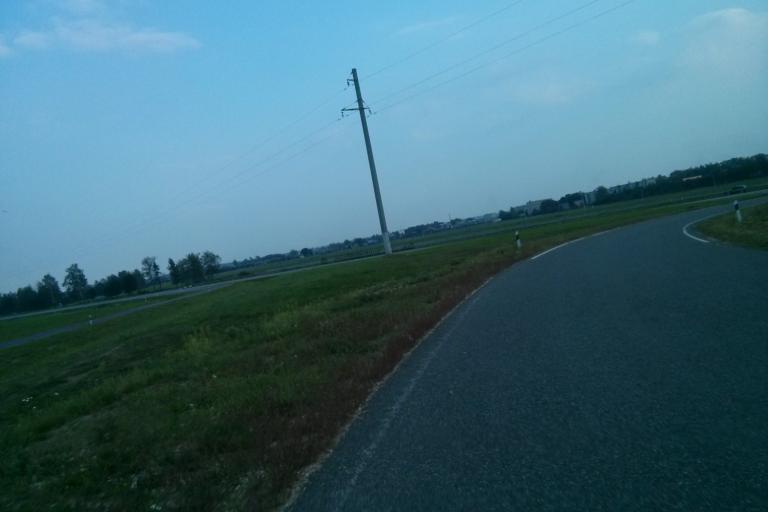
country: BY
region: Minsk
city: Chervyen'
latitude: 53.7254
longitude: 28.3954
